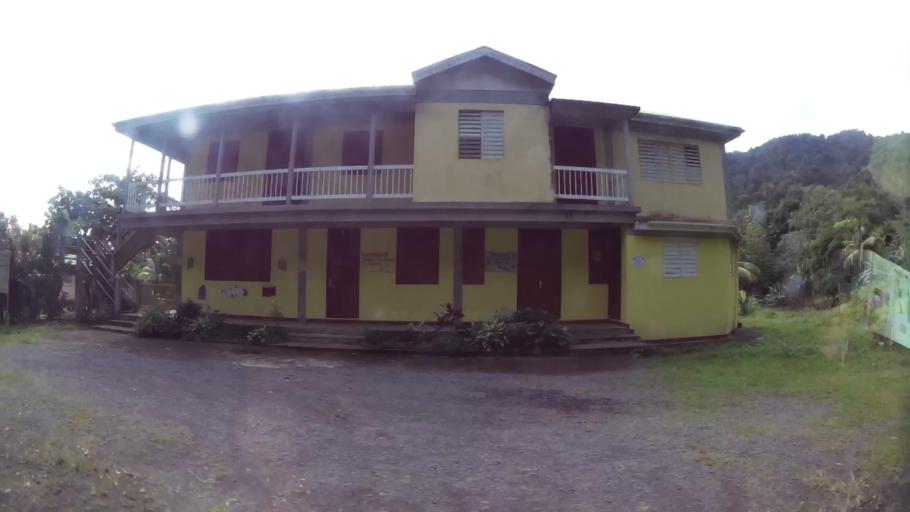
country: DM
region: Saint David
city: Castle Bruce
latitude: 15.4659
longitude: -61.2538
